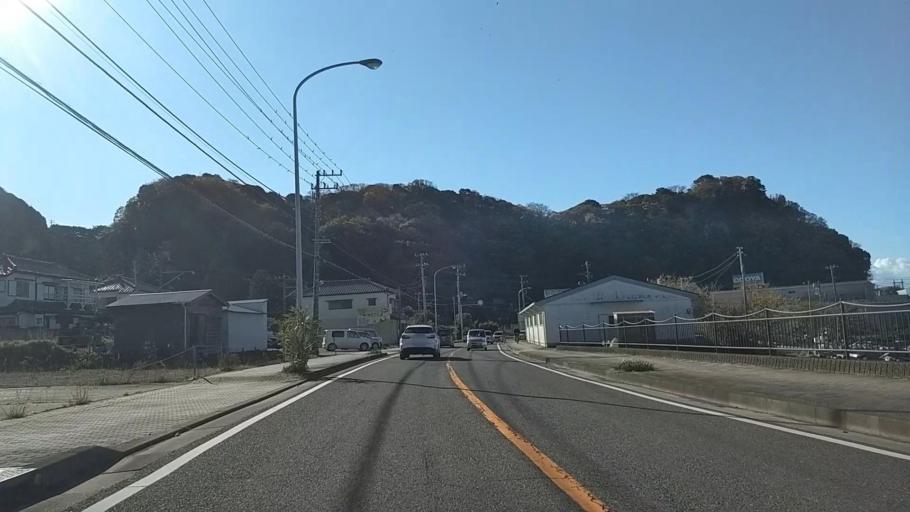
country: JP
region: Chiba
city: Tateyama
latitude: 35.1300
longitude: 139.8397
